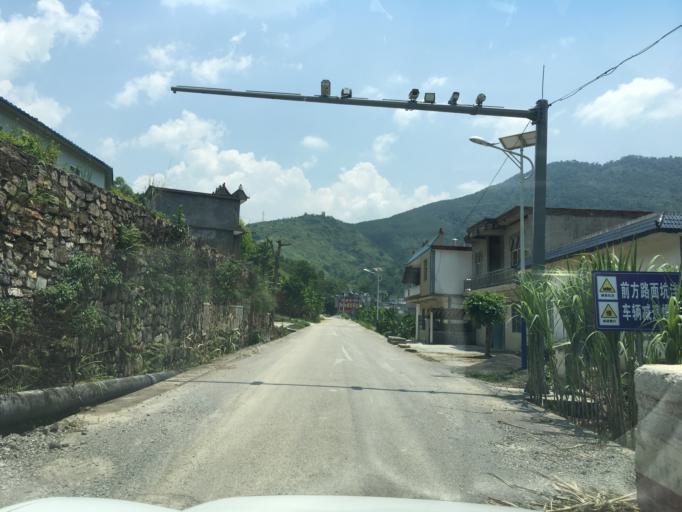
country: CN
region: Guangxi Zhuangzu Zizhiqu
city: Xinzhou
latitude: 24.9091
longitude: 105.4673
